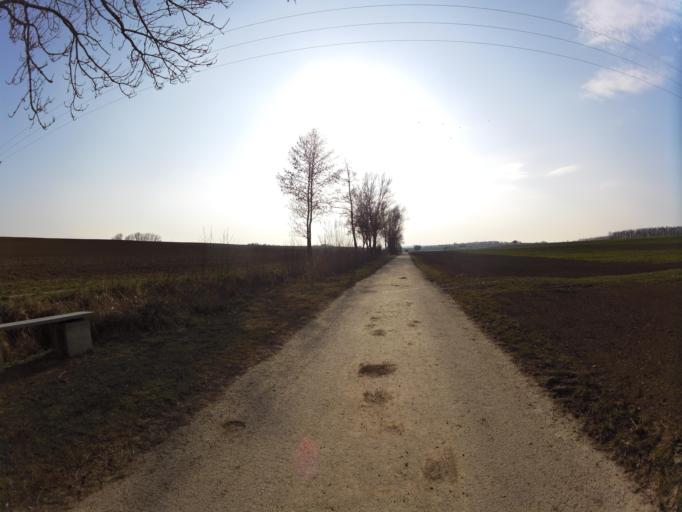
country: DE
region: Bavaria
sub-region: Regierungsbezirk Unterfranken
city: Giebelstadt
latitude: 49.6549
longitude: 9.9299
